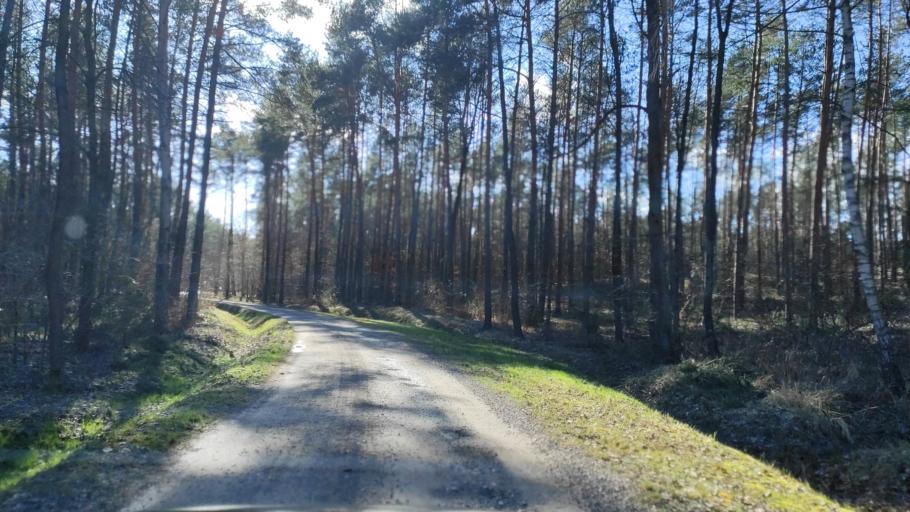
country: PL
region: Masovian Voivodeship
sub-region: Powiat radomski
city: Jastrzebia
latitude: 51.4714
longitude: 21.2433
